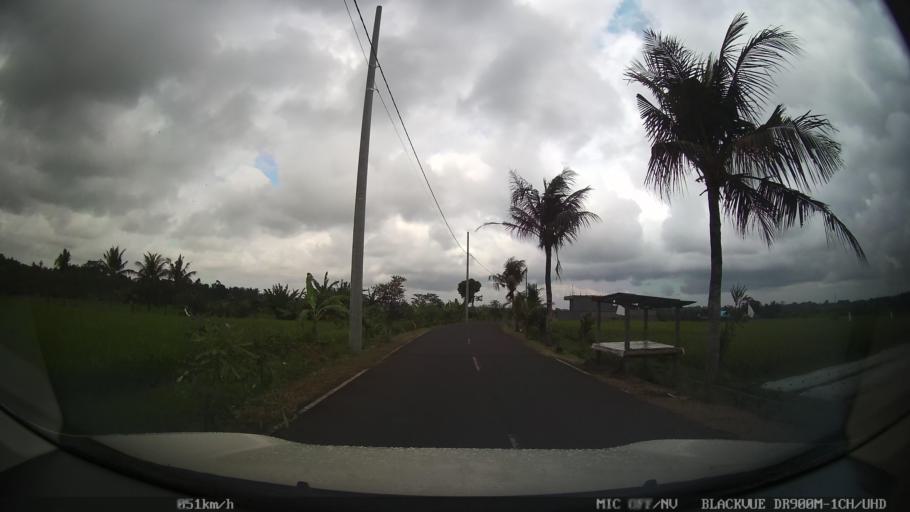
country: ID
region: Bali
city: Banjar Cemenggon
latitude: -8.5333
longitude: 115.1891
